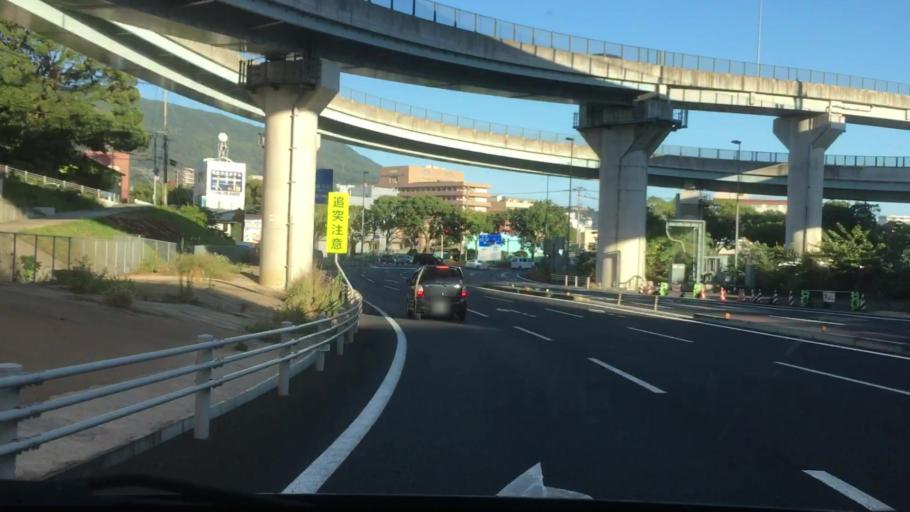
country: JP
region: Nagasaki
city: Sasebo
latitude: 33.1731
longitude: 129.7118
